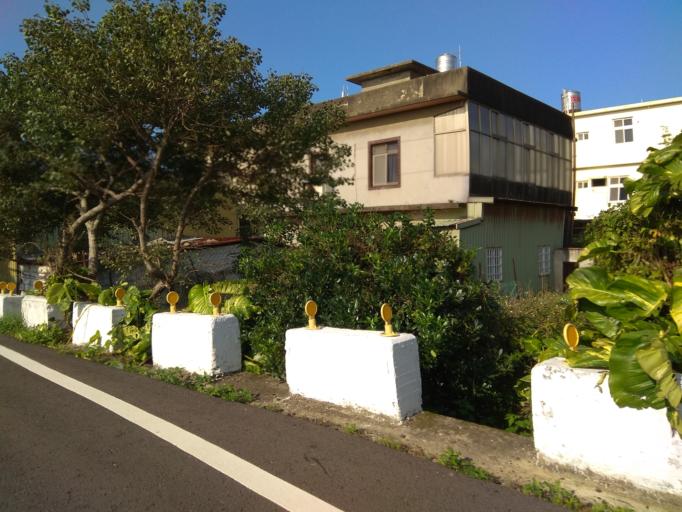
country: TW
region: Taiwan
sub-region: Hsinchu
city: Zhubei
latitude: 25.0013
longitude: 121.0455
